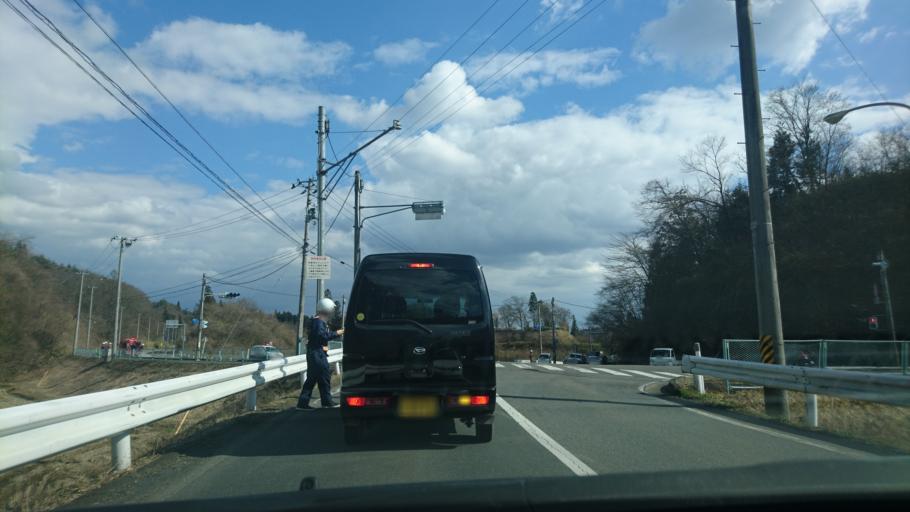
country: JP
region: Iwate
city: Kitakami
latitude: 39.3012
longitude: 141.2024
